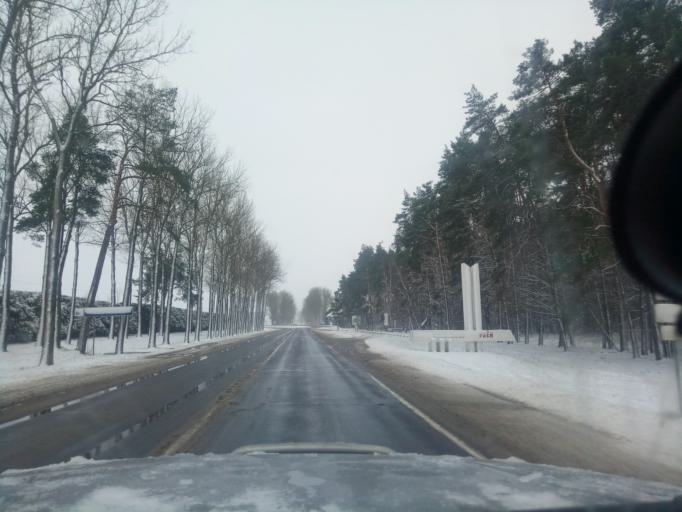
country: BY
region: Minsk
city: Haradzyeya
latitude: 53.3382
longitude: 26.5211
